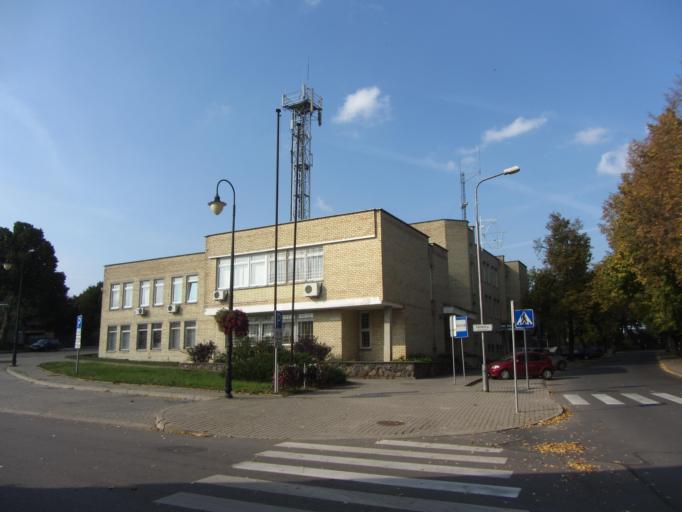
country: LT
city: Trakai
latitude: 54.6392
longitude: 24.9334
